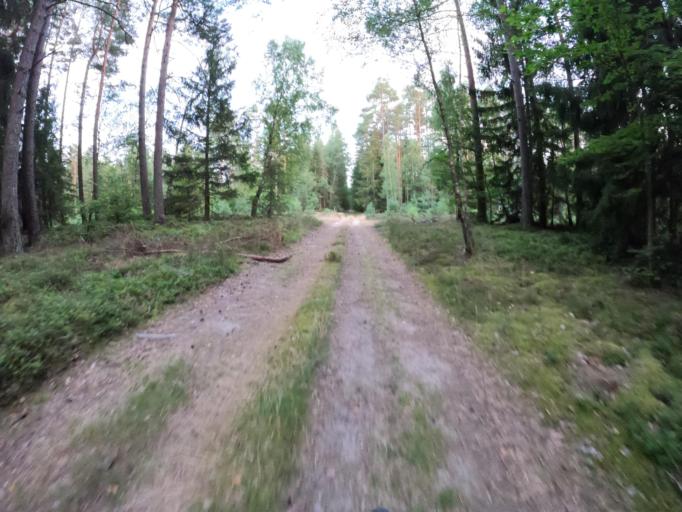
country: PL
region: West Pomeranian Voivodeship
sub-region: Powiat koszalinski
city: Sianow
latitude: 54.0898
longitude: 16.4083
